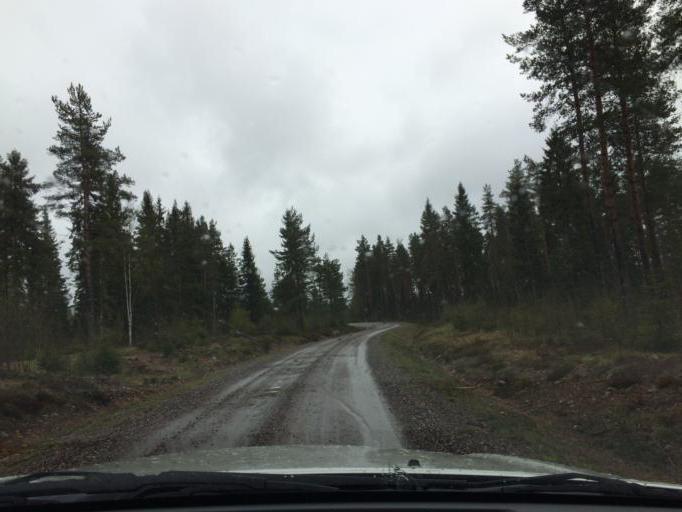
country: SE
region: OErebro
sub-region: Hallefors Kommun
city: Haellefors
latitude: 60.0361
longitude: 14.5320
